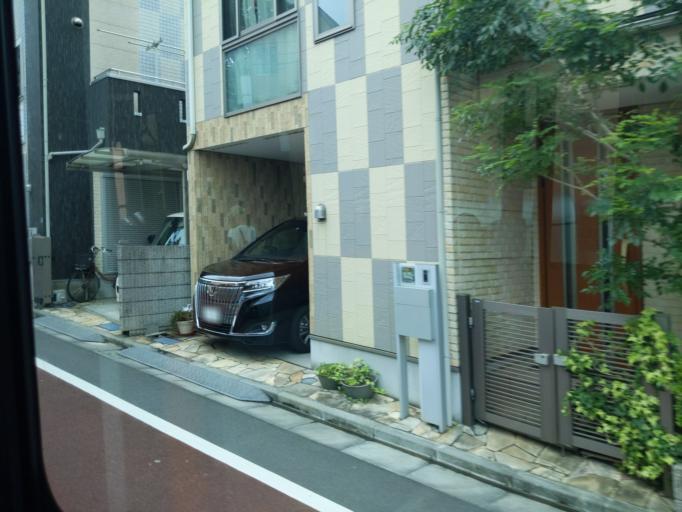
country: JP
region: Saitama
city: Wako
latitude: 35.7810
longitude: 139.6465
